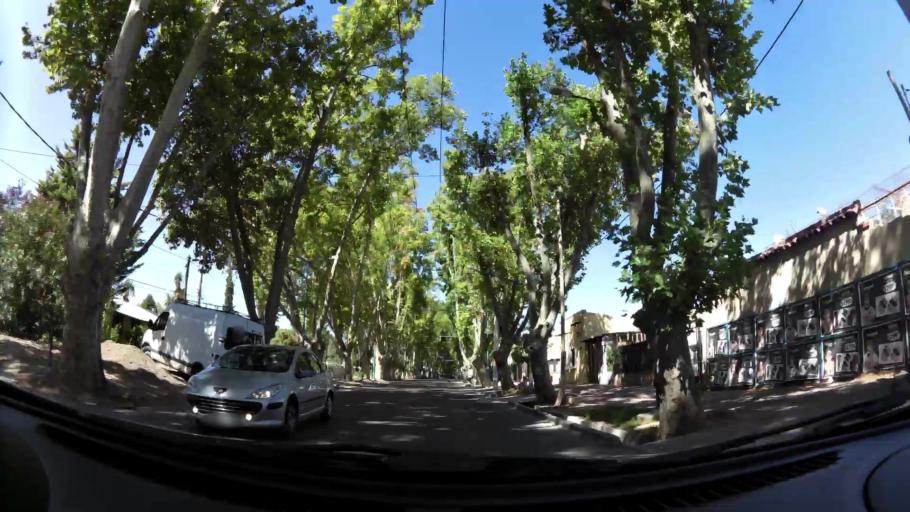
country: AR
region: Mendoza
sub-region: Departamento de Godoy Cruz
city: Godoy Cruz
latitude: -32.9430
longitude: -68.8418
